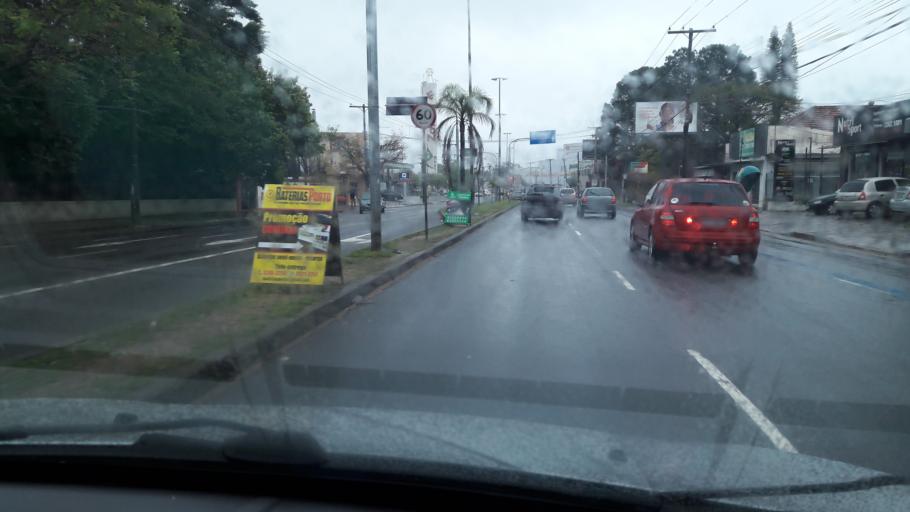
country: BR
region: Rio Grande do Sul
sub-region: Porto Alegre
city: Porto Alegre
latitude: -30.1103
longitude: -51.2269
